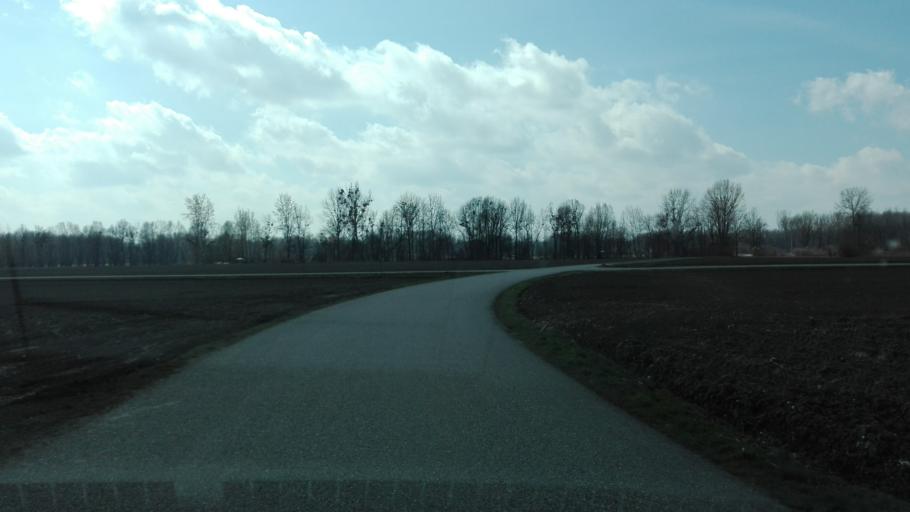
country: AT
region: Upper Austria
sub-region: Politischer Bezirk Urfahr-Umgebung
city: Goldworth
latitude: 48.3278
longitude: 14.0920
